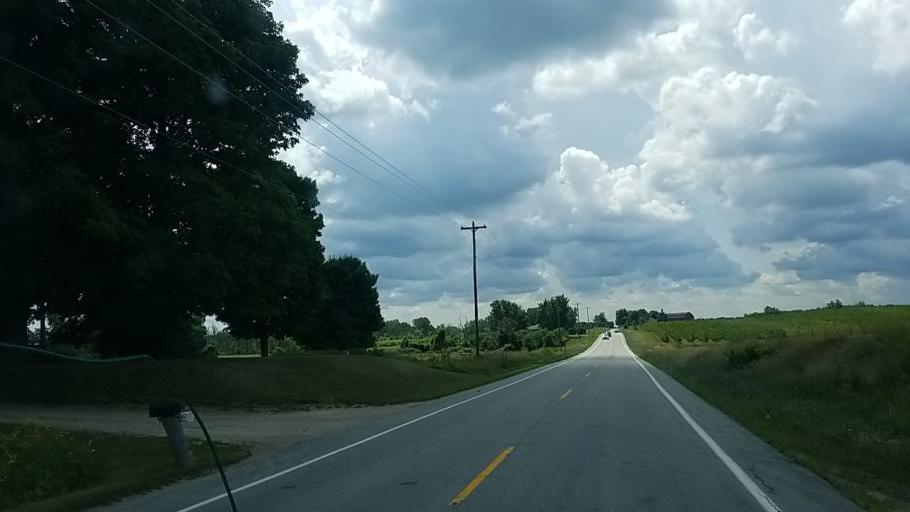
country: US
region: Michigan
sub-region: Kent County
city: Walker
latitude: 43.0798
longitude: -85.7681
